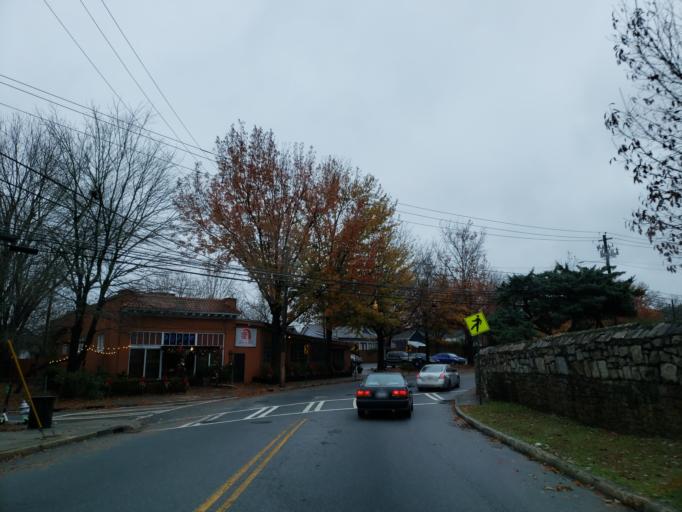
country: US
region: Georgia
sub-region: Fulton County
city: Atlanta
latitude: 33.7481
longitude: -84.3684
